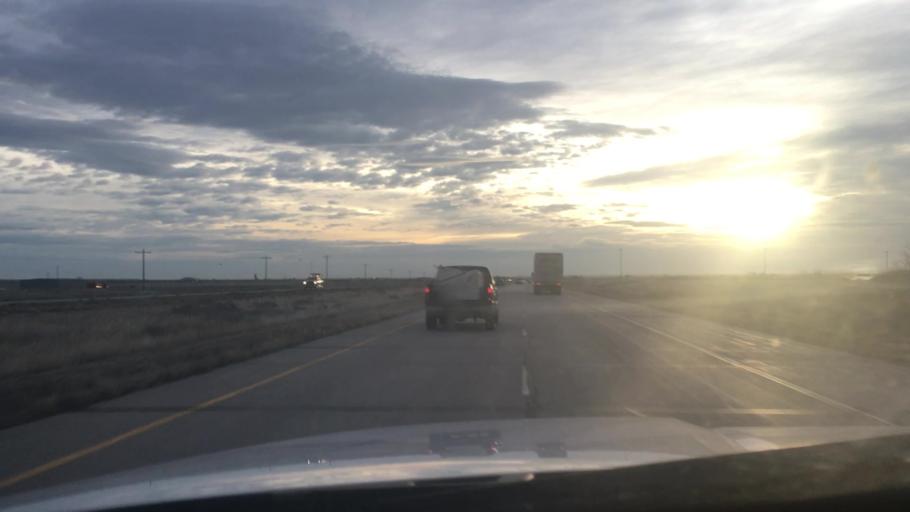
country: US
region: Colorado
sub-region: Morgan County
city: Fort Morgan
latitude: 40.2489
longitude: -104.0033
